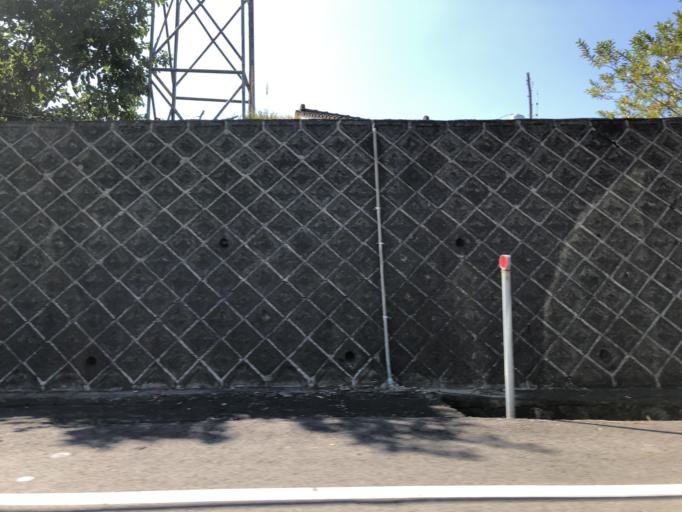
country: TW
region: Taiwan
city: Yujing
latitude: 23.0580
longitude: 120.3974
